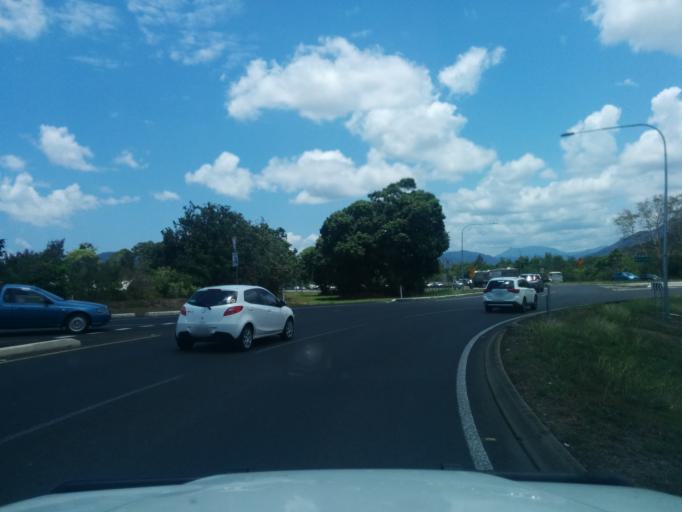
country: AU
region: Queensland
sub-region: Cairns
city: Redlynch
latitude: -16.8400
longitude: 145.6934
